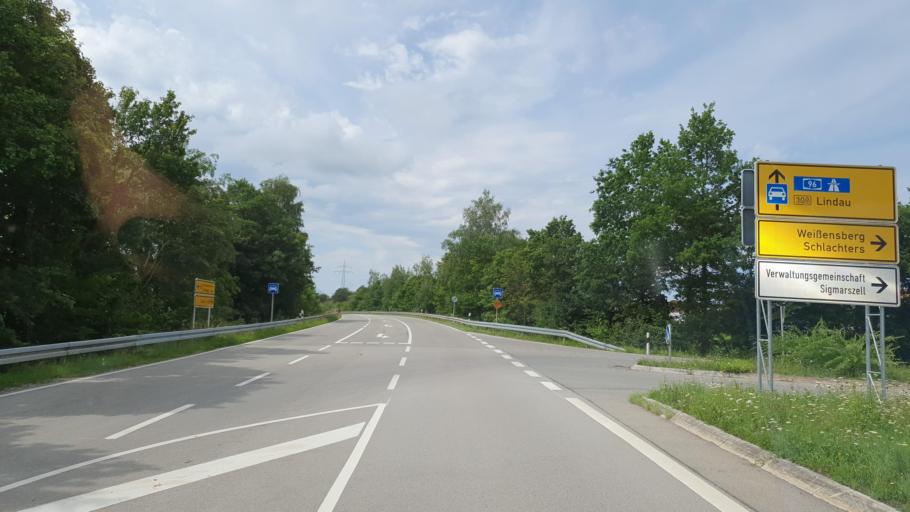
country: DE
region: Bavaria
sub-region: Swabia
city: Sigmarszell
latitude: 47.5902
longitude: 9.7541
